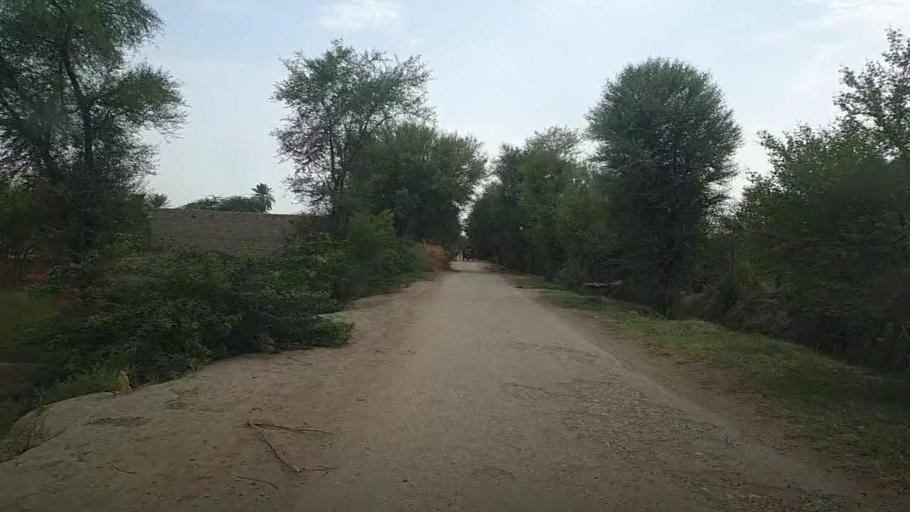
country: PK
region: Sindh
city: Karaundi
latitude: 26.9517
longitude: 68.4150
